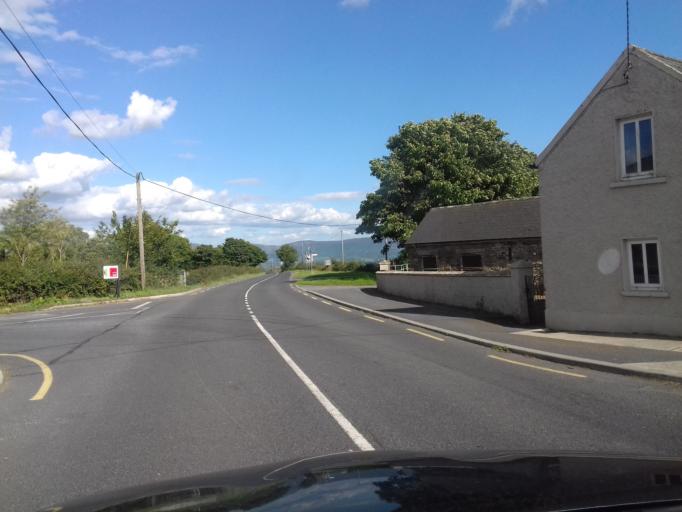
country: IE
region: Leinster
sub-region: Kilkenny
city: Graiguenamanagh
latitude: 52.5471
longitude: -7.0267
